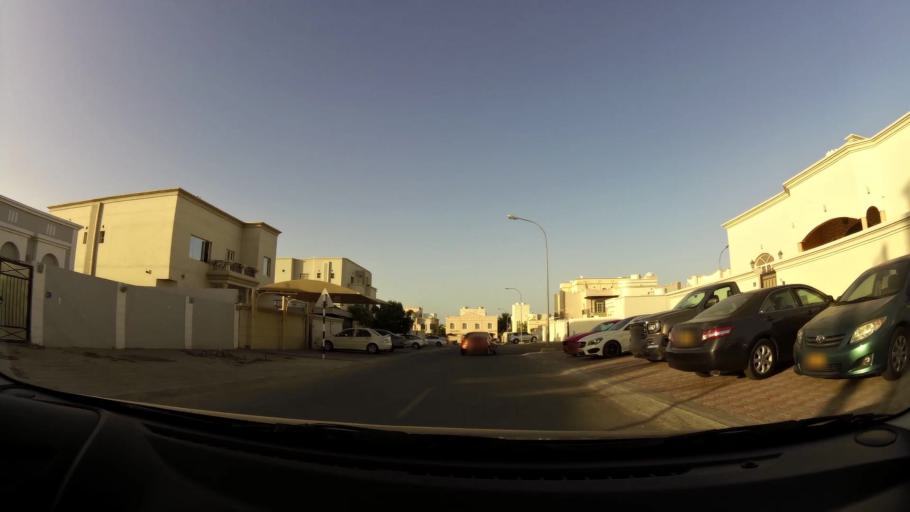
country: OM
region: Muhafazat Masqat
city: As Sib al Jadidah
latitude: 23.6043
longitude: 58.2263
